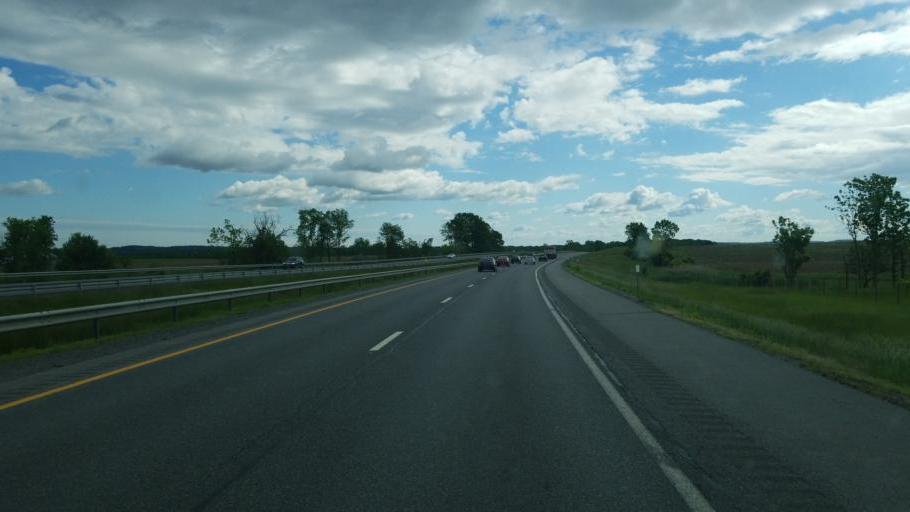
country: US
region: New York
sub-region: Seneca County
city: Seneca Falls
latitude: 42.9800
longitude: -76.7976
